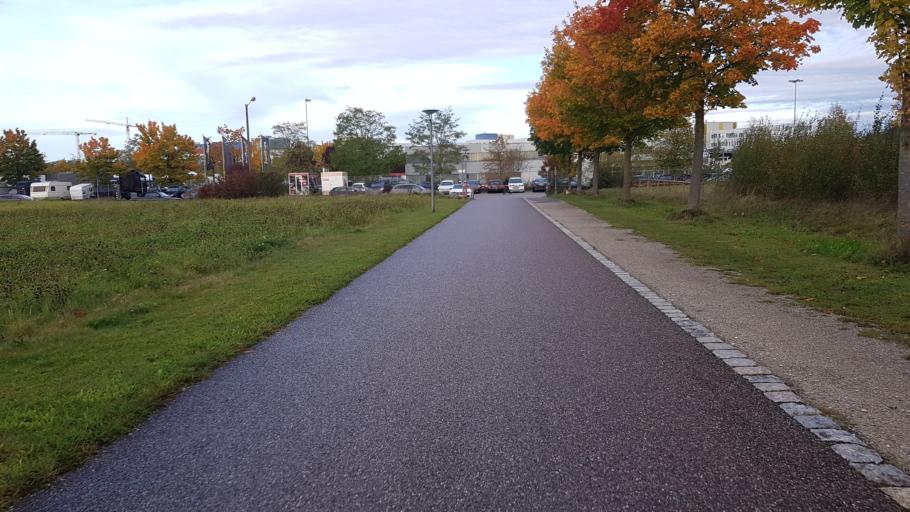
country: DE
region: Bavaria
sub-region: Upper Bavaria
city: Neubiberg
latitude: 48.0884
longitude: 11.6567
